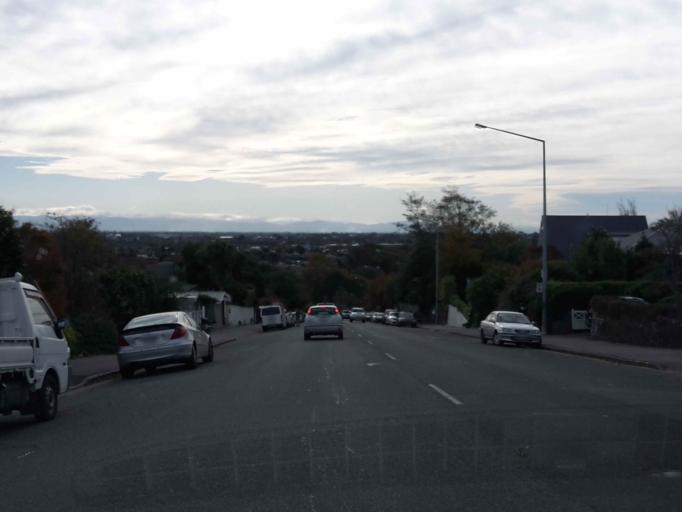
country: NZ
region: Canterbury
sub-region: Christchurch City
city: Christchurch
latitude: -43.5723
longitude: 172.6244
